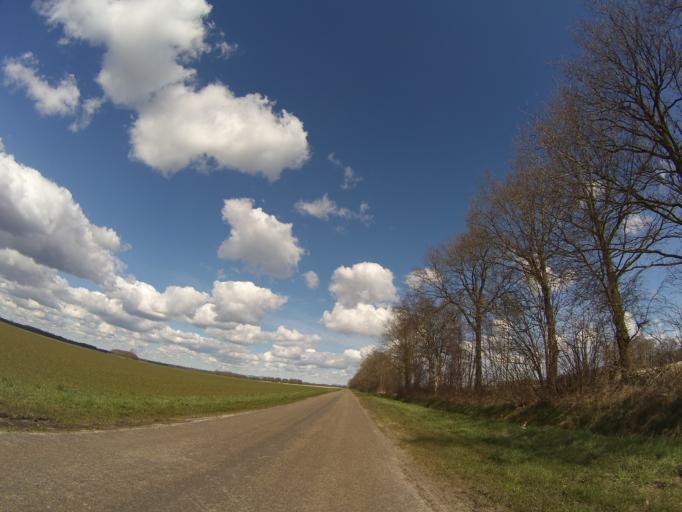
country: NL
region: Drenthe
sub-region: Gemeente Coevorden
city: Sleen
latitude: 52.7693
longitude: 6.8386
